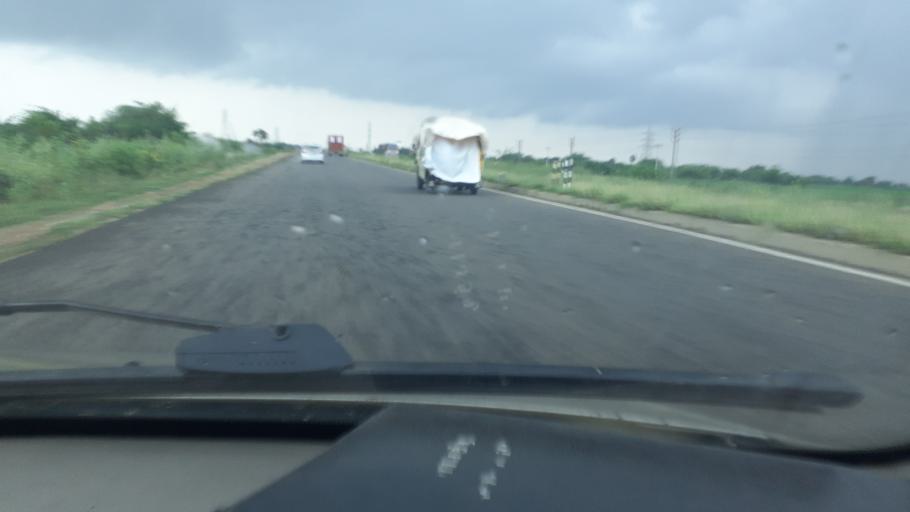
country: IN
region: Tamil Nadu
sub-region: Thoothukkudi
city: Kovilpatti
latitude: 9.1062
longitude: 77.8092
